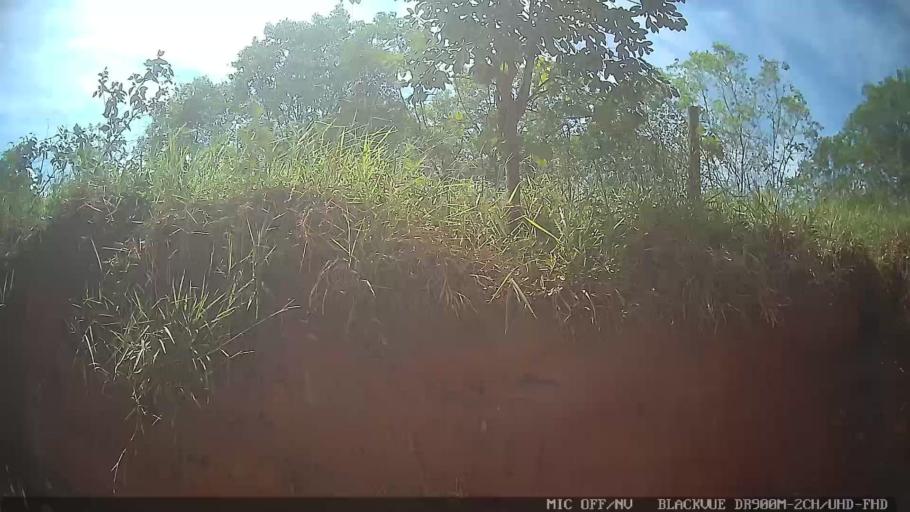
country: BR
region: Sao Paulo
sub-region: Braganca Paulista
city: Braganca Paulista
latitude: -22.9838
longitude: -46.6449
